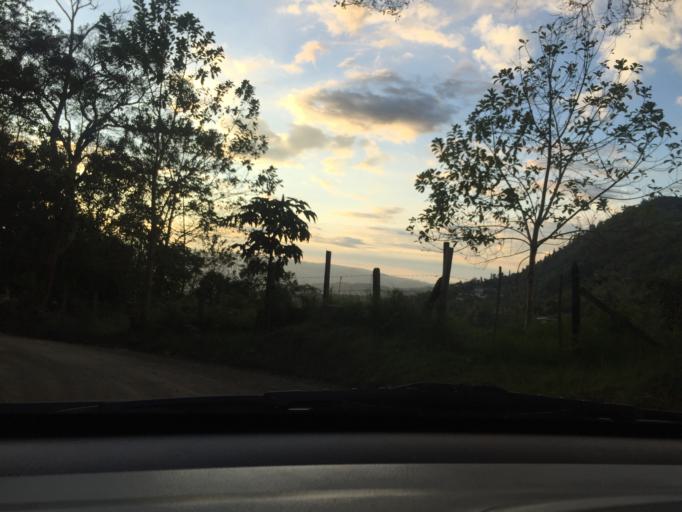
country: CO
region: Cundinamarca
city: Zipacon
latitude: 4.7092
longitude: -74.4010
